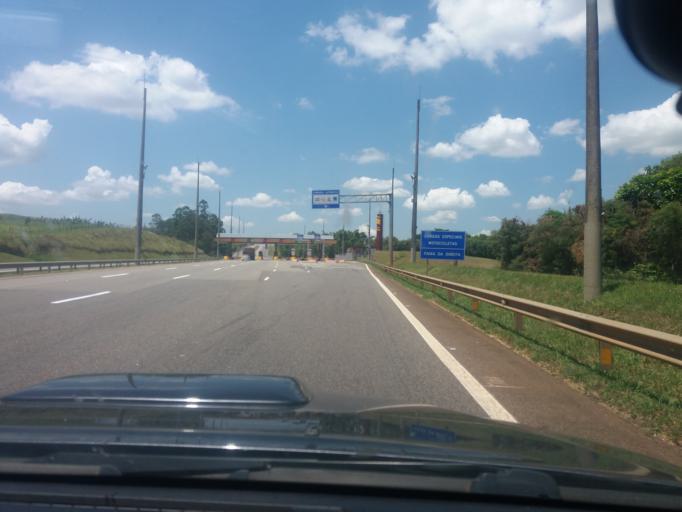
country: BR
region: Sao Paulo
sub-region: Itapetininga
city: Itapetininga
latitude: -23.4695
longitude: -47.9670
